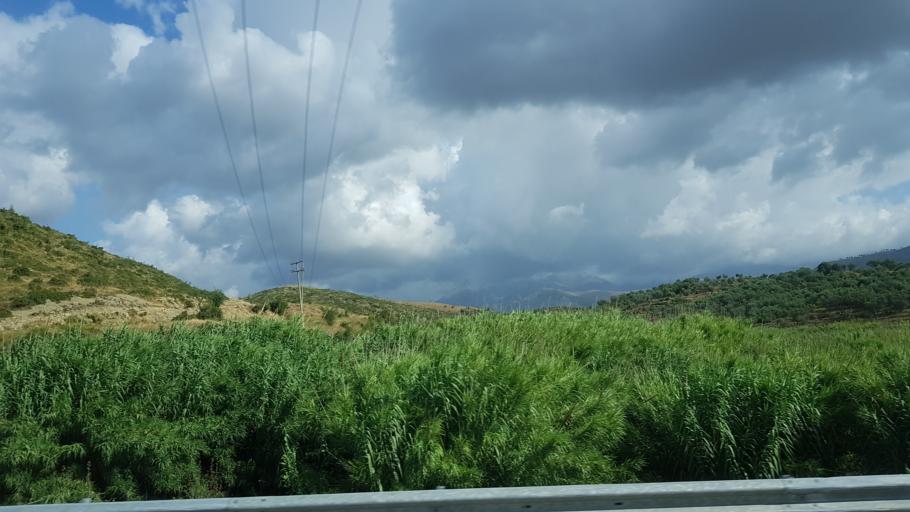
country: AL
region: Vlore
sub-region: Rrethi i Delvines
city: Mesopotam
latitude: 39.9007
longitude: 20.0805
